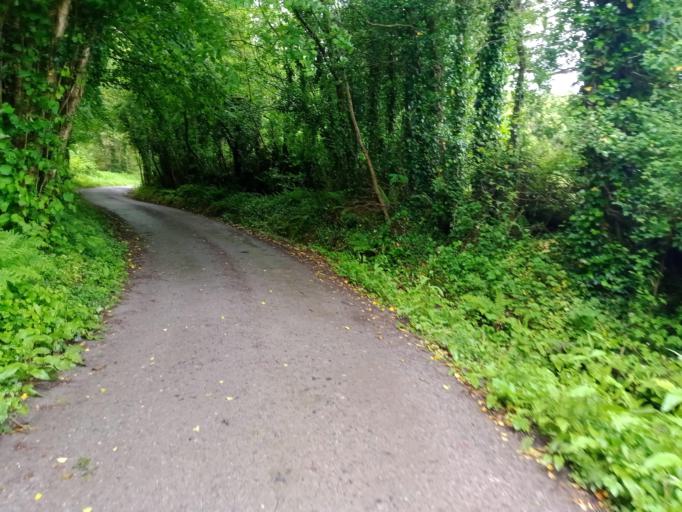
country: IE
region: Leinster
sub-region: Kilkenny
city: Thomastown
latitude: 52.4779
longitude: -7.0504
